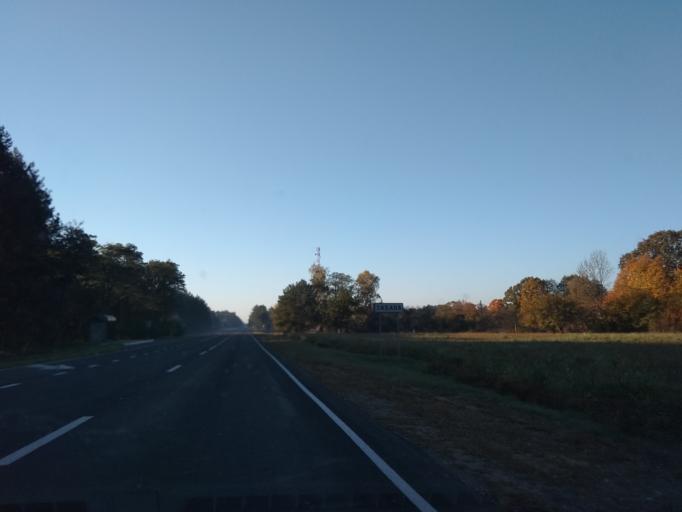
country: BY
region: Brest
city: Kobryn
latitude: 52.0560
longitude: 24.2801
